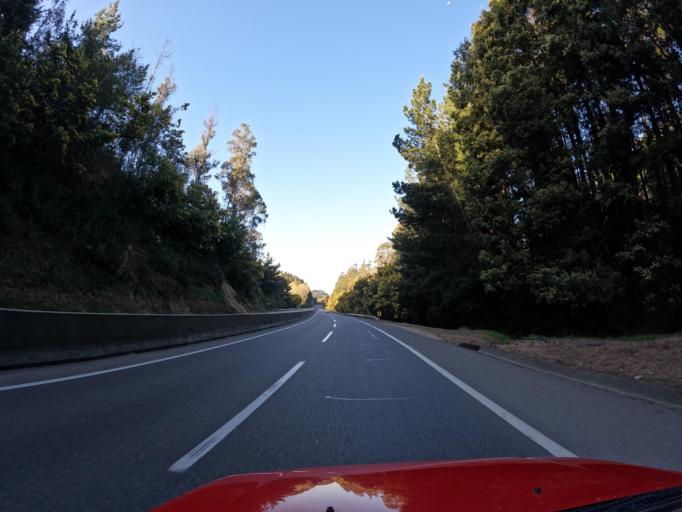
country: CL
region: Biobio
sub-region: Provincia de Concepcion
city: Penco
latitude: -36.7312
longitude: -72.8467
